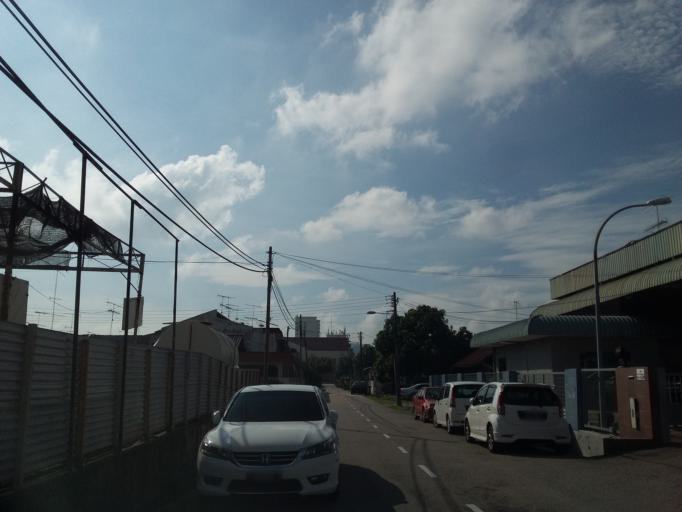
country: MY
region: Johor
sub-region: Daerah Batu Pahat
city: Batu Pahat
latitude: 1.8584
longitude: 102.9306
